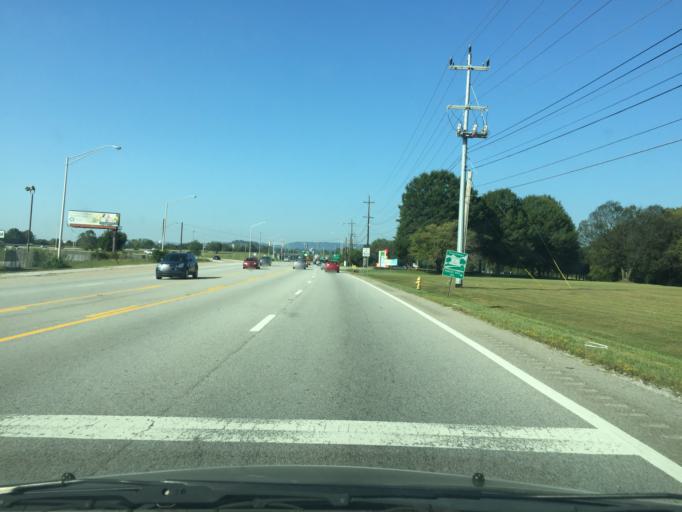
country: US
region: Tennessee
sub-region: Hamilton County
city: East Chattanooga
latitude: 35.0964
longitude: -85.2433
